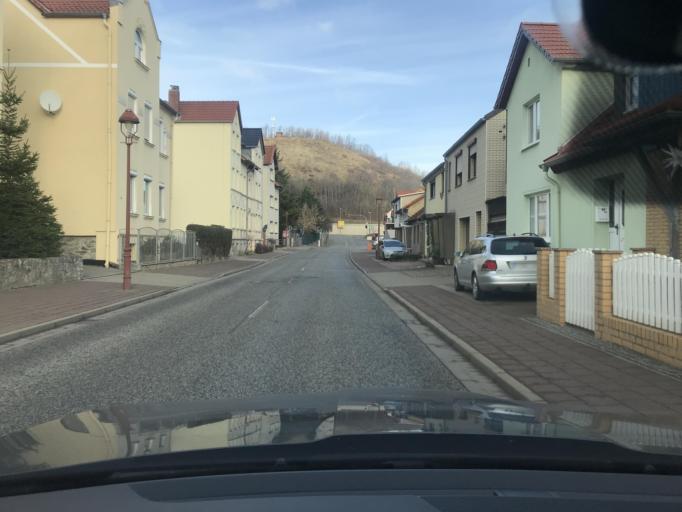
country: DE
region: Saxony-Anhalt
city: Thale
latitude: 51.7565
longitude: 11.0363
